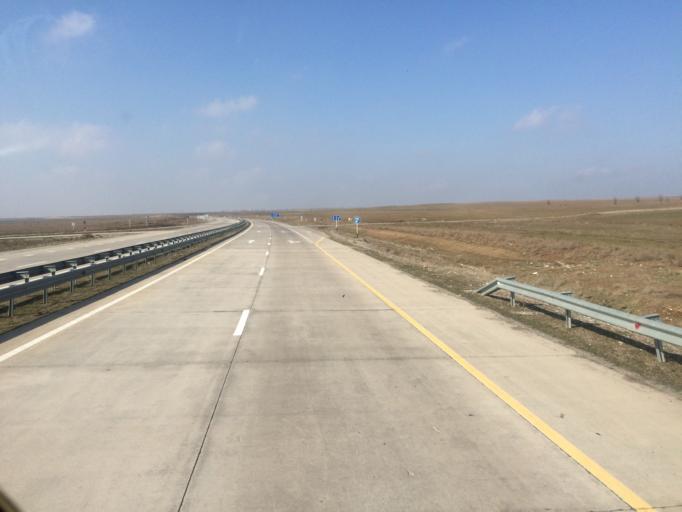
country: KZ
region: Ongtustik Qazaqstan
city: Shymkent
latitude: 42.4876
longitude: 69.5199
